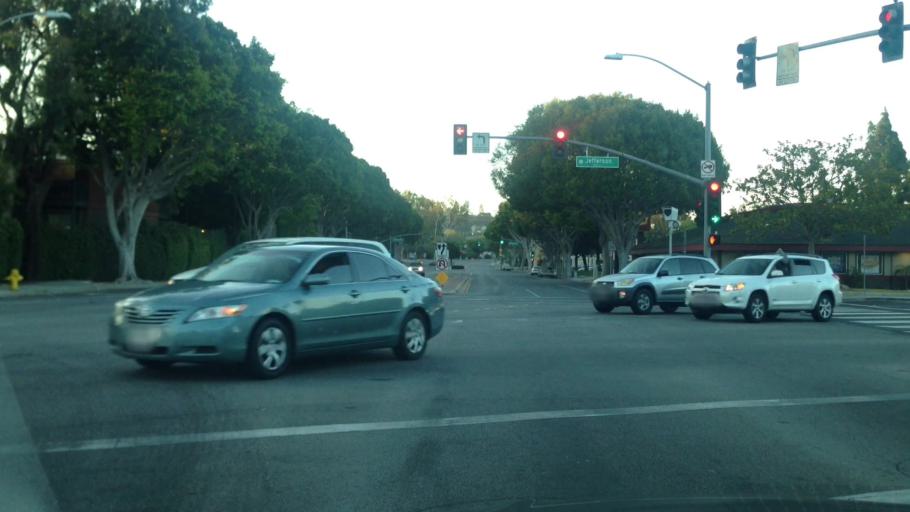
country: US
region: California
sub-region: Los Angeles County
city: Culver City
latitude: 34.0043
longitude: -118.3937
